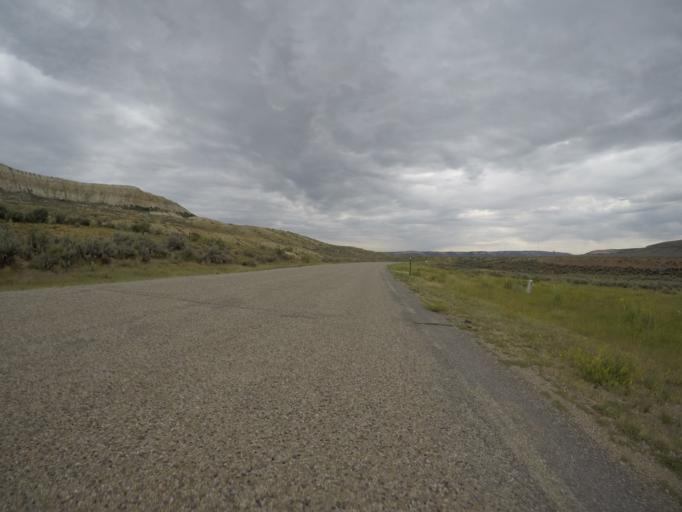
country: US
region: Wyoming
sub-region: Lincoln County
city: Kemmerer
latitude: 41.8230
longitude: -110.7358
